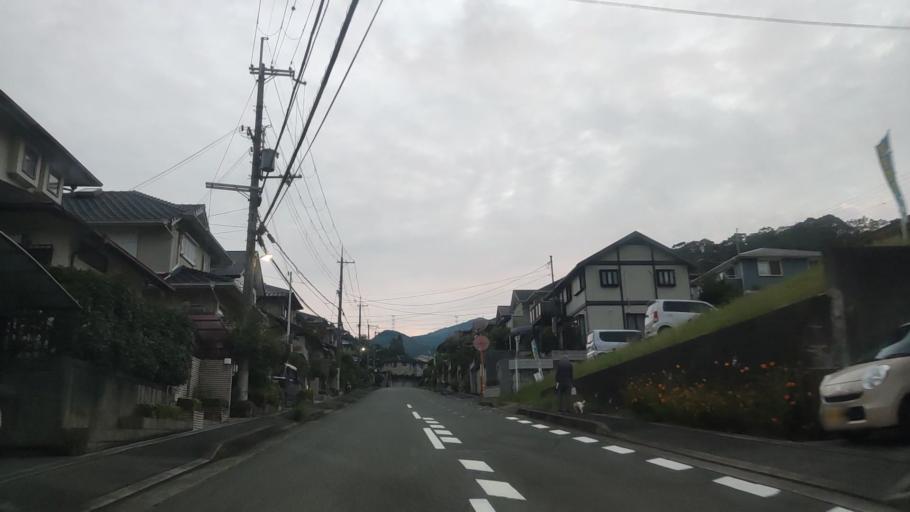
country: JP
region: Wakayama
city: Hashimoto
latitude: 34.3688
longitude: 135.6063
